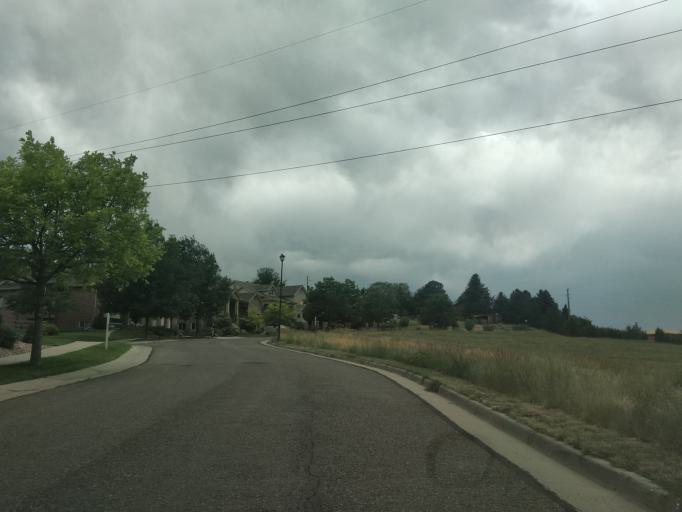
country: US
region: Colorado
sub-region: Jefferson County
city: Lakewood
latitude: 39.7000
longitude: -105.0860
